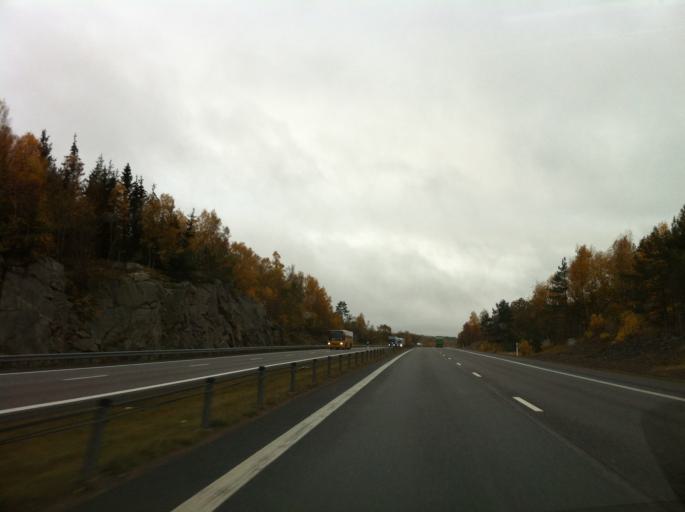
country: SE
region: Joenkoeping
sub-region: Jonkopings Kommun
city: Graenna
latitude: 58.0422
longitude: 14.4991
